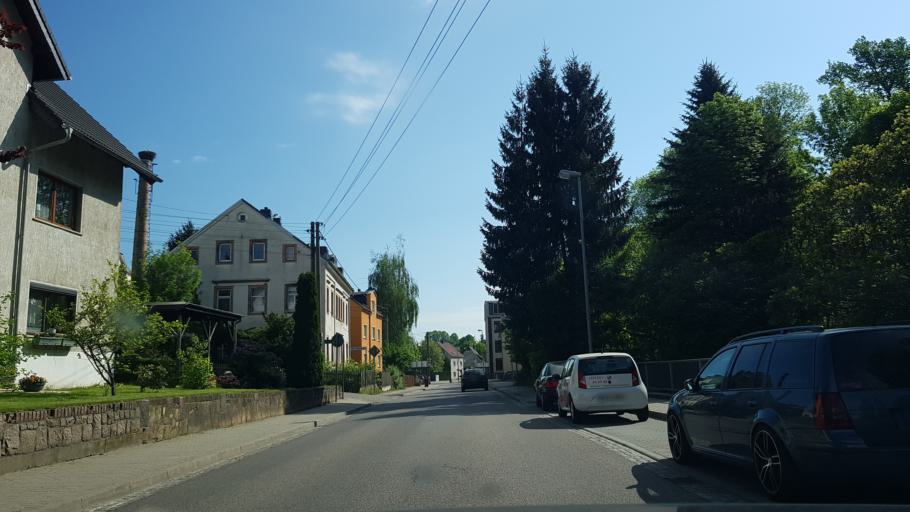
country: DE
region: Saxony
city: Wittgensdorf
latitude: 50.8804
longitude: 12.8657
